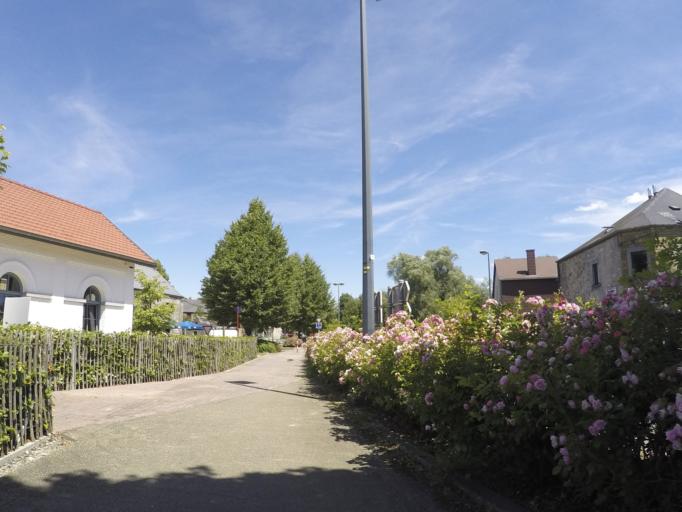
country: BE
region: Wallonia
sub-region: Province de Namur
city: Hamois
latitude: 50.3403
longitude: 5.1556
